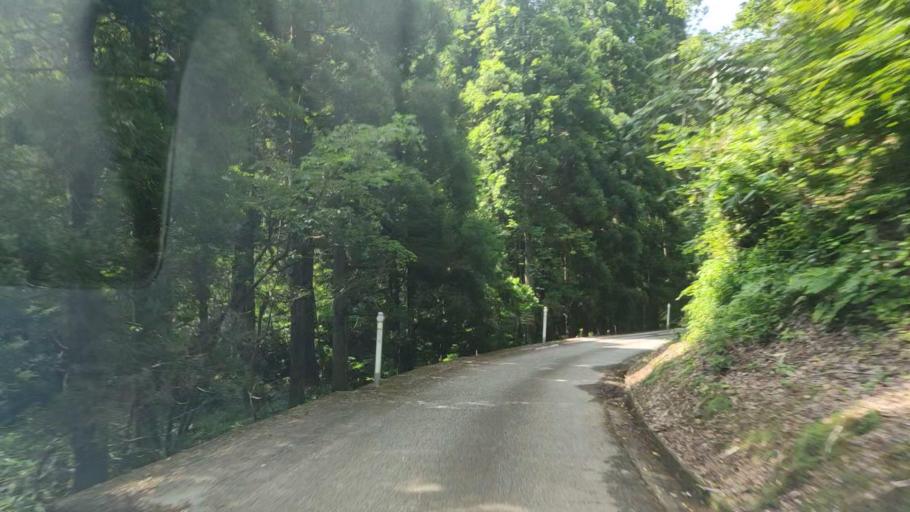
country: JP
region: Ishikawa
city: Komatsu
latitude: 36.2685
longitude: 136.5343
